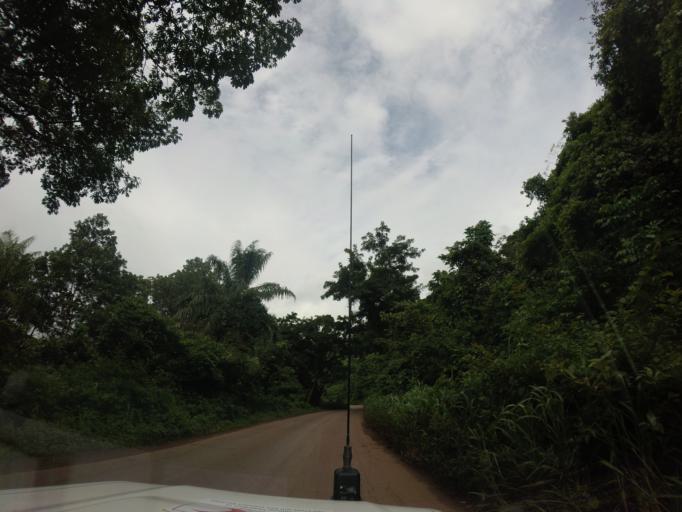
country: GN
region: Kindia
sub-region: Coyah
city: Coyah
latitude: 9.7424
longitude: -13.3668
